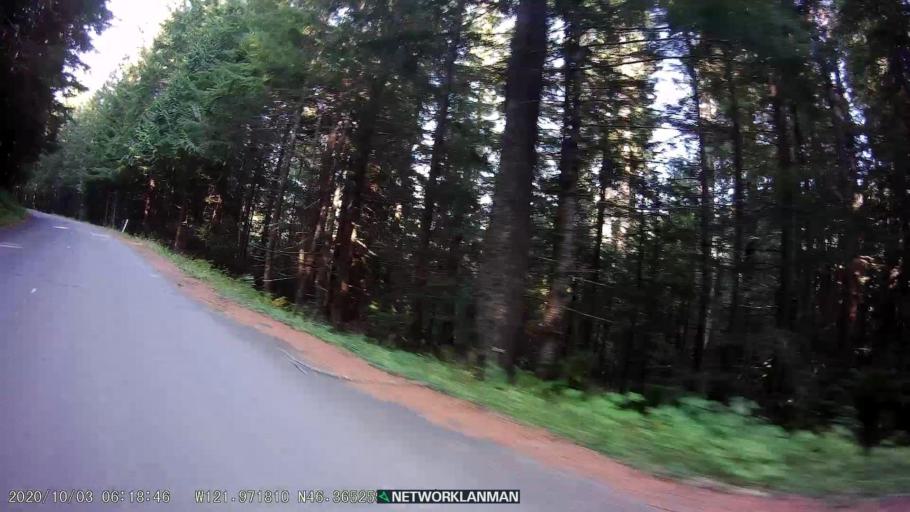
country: US
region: Washington
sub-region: Lewis County
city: Morton
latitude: 46.3655
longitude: -121.9719
